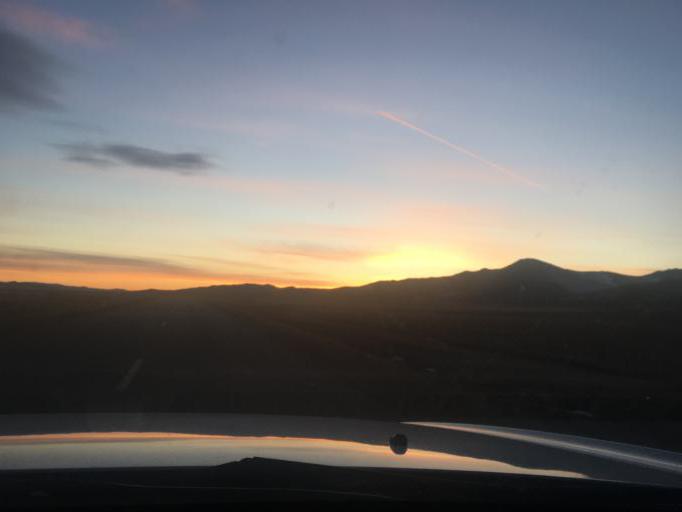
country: MN
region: Central Aimak
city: Mandal
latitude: 48.0924
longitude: 106.6057
